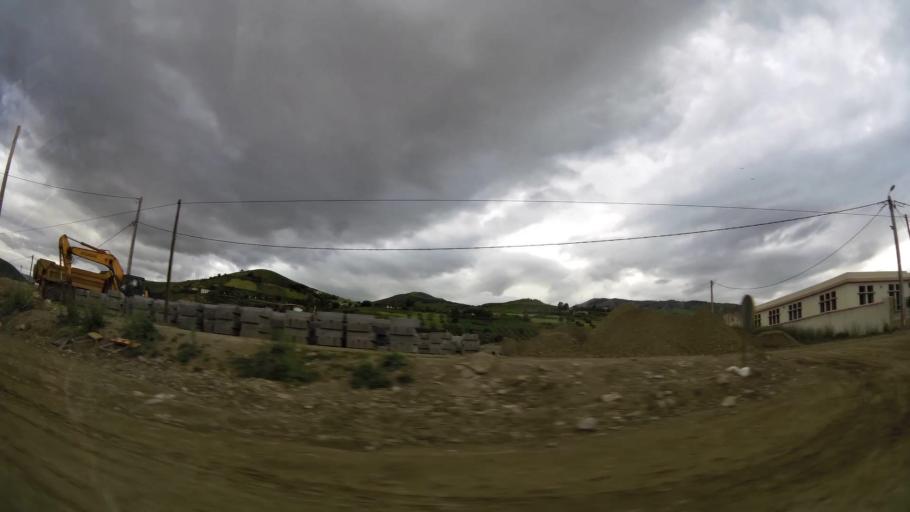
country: MA
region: Taza-Al Hoceima-Taounate
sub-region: Taza
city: Taza
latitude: 34.3527
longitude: -3.9209
